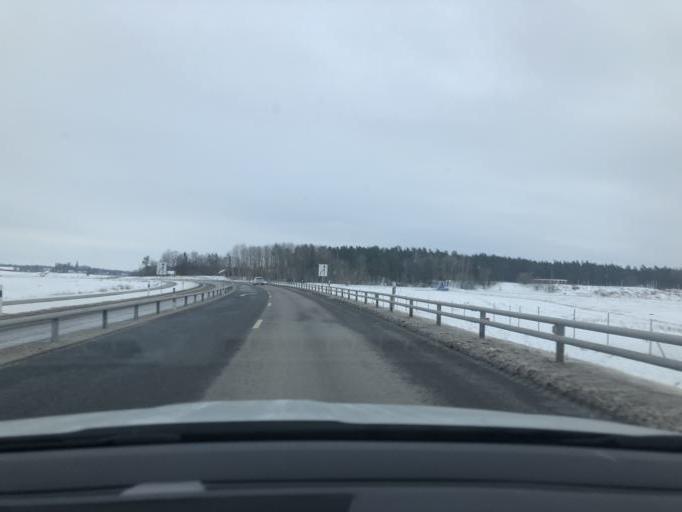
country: SE
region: OEstergoetland
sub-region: Linkopings Kommun
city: Sturefors
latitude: 58.3971
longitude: 15.7197
